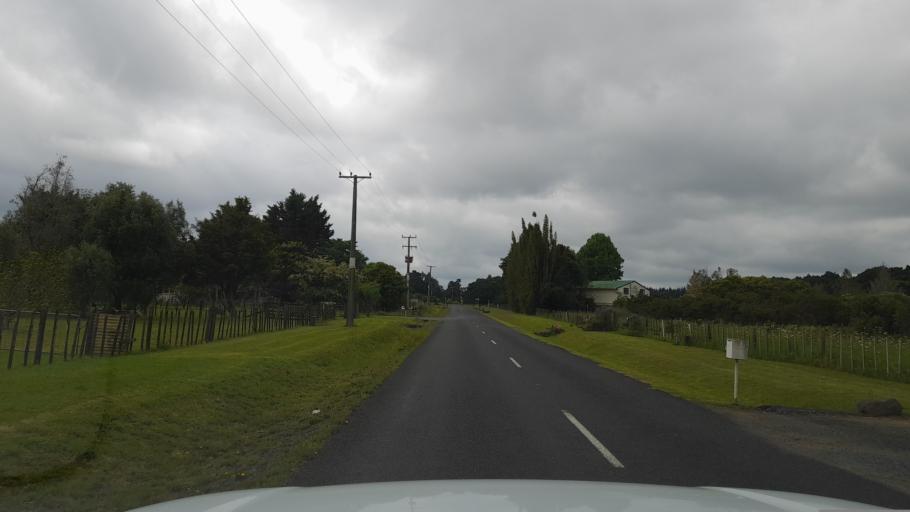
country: NZ
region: Northland
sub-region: Far North District
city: Waimate North
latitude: -35.4214
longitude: 173.7948
